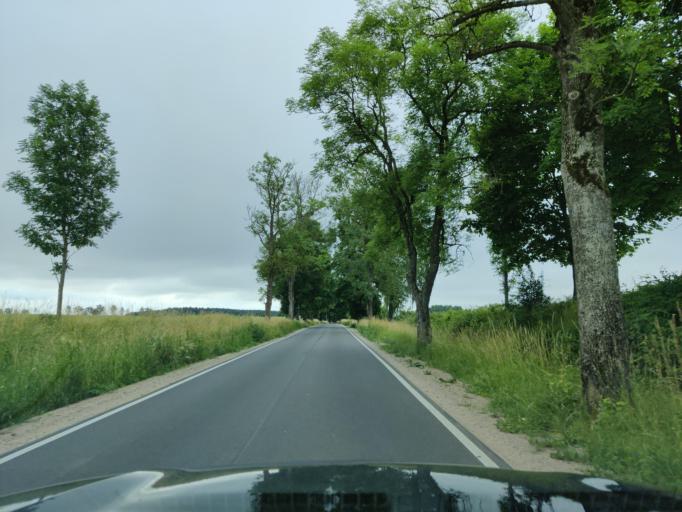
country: PL
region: Warmian-Masurian Voivodeship
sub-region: Powiat gizycki
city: Ryn
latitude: 53.9088
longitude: 21.5616
